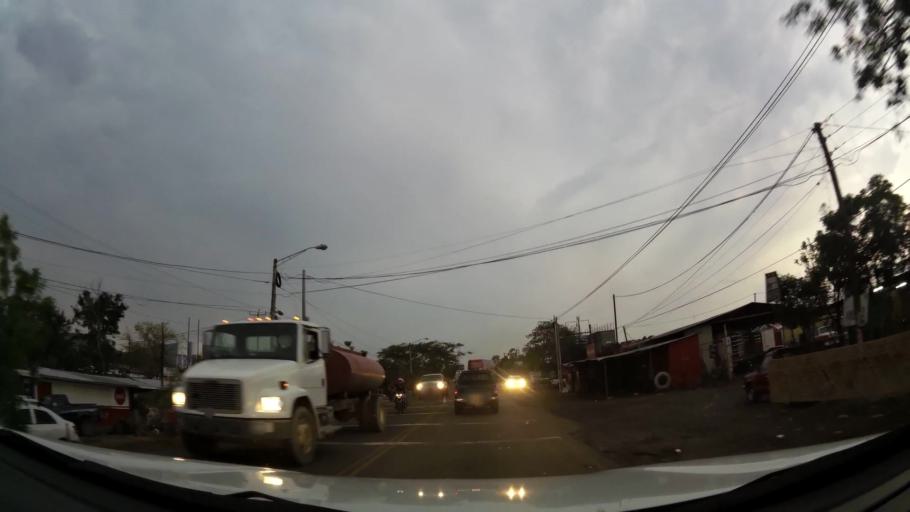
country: NI
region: Esteli
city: Esteli
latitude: 13.0663
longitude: -86.3483
